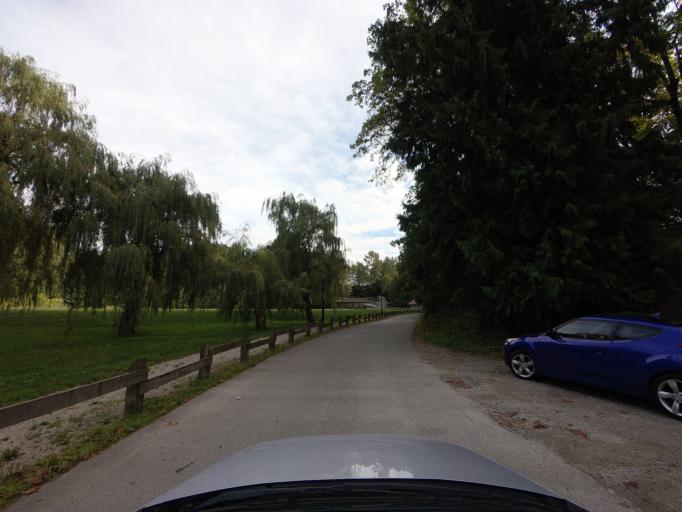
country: CA
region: British Columbia
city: New Westminster
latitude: 49.2366
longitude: -122.8921
